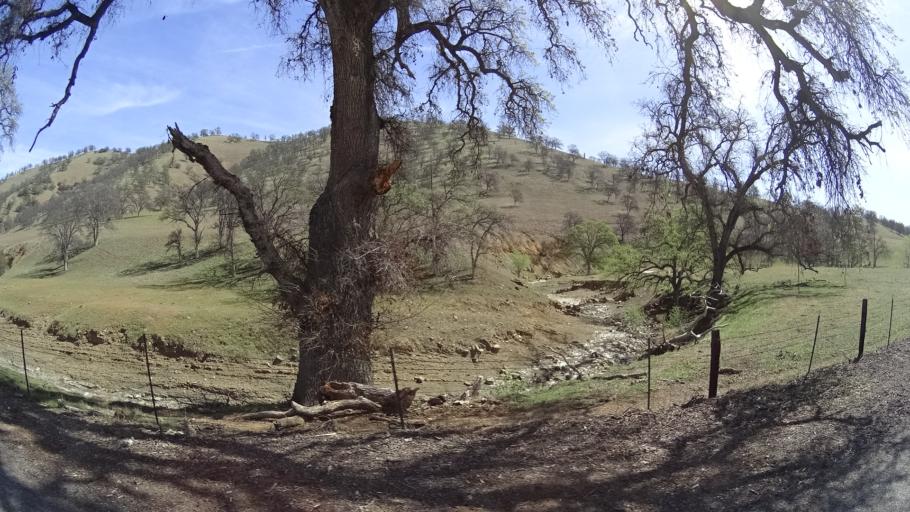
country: US
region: California
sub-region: Glenn County
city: Willows
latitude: 39.5242
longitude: -122.4575
